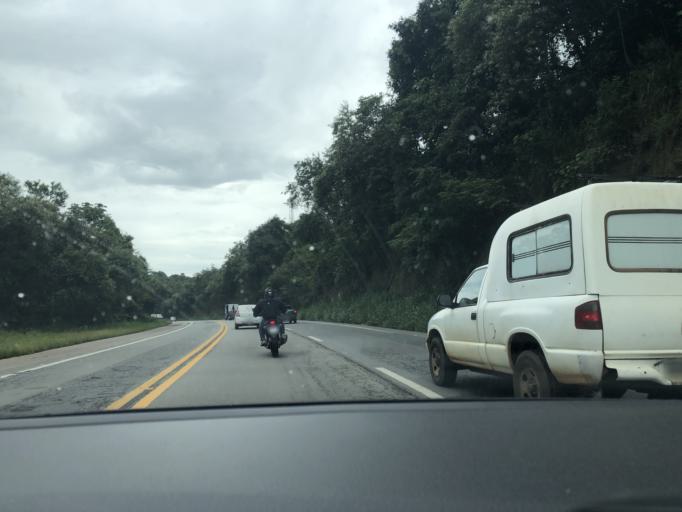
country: BR
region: Sao Paulo
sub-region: Jarinu
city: Jarinu
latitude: -23.1573
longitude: -46.7477
